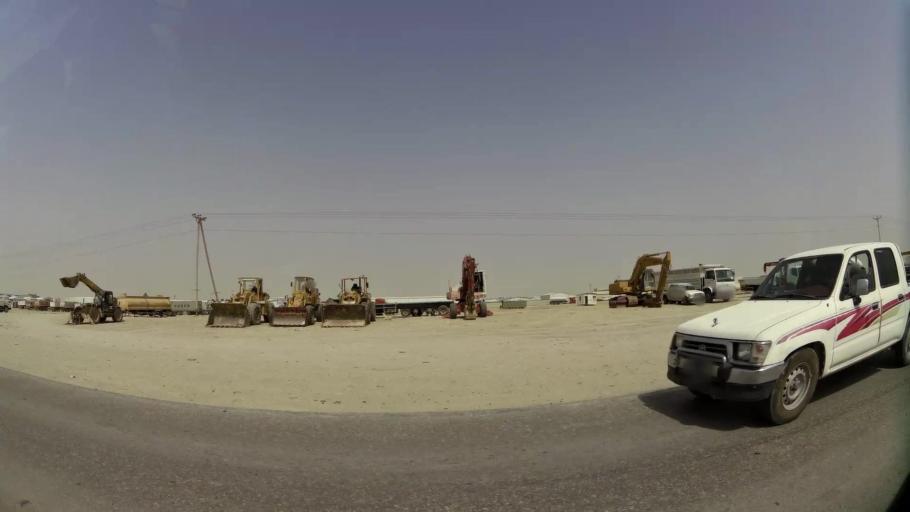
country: QA
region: Baladiyat ar Rayyan
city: Ar Rayyan
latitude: 25.2090
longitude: 51.3599
